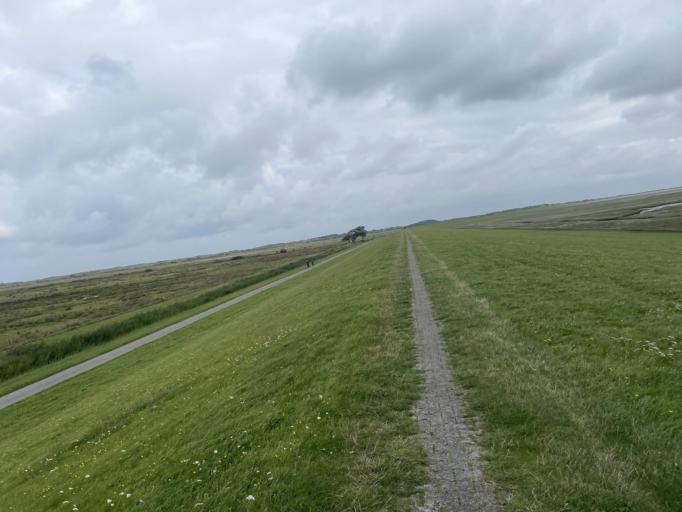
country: DE
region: Lower Saxony
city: Borkum
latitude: 53.5913
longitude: 6.7389
